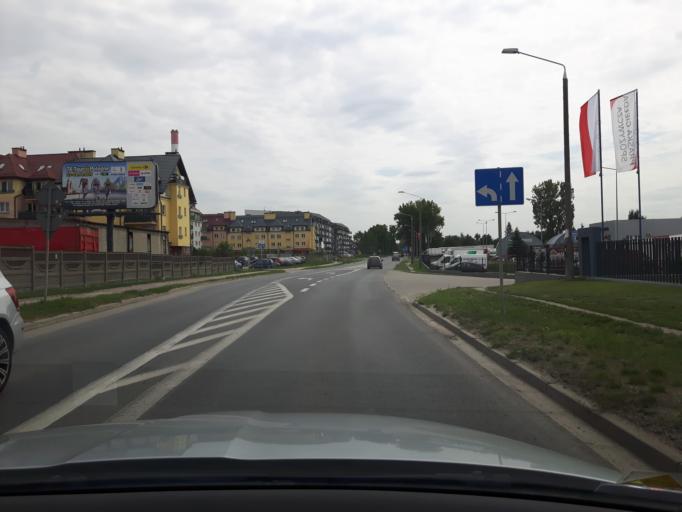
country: PL
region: Masovian Voivodeship
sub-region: Powiat wolominski
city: Zabki
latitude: 52.2771
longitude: 21.1157
